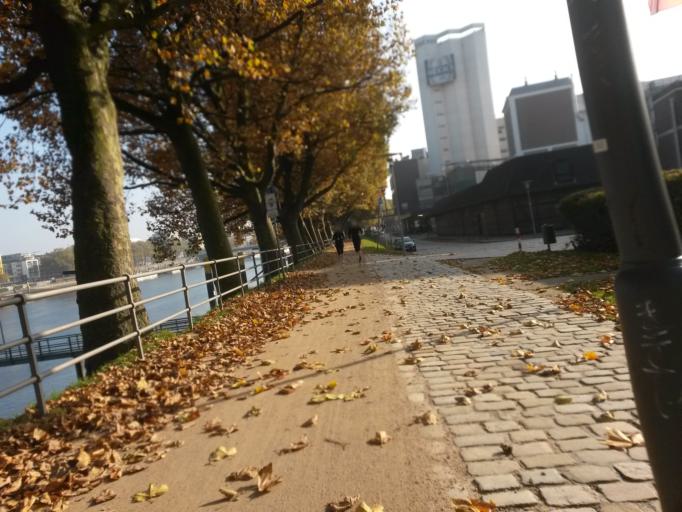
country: DE
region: Bremen
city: Bremen
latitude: 53.0789
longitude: 8.7908
